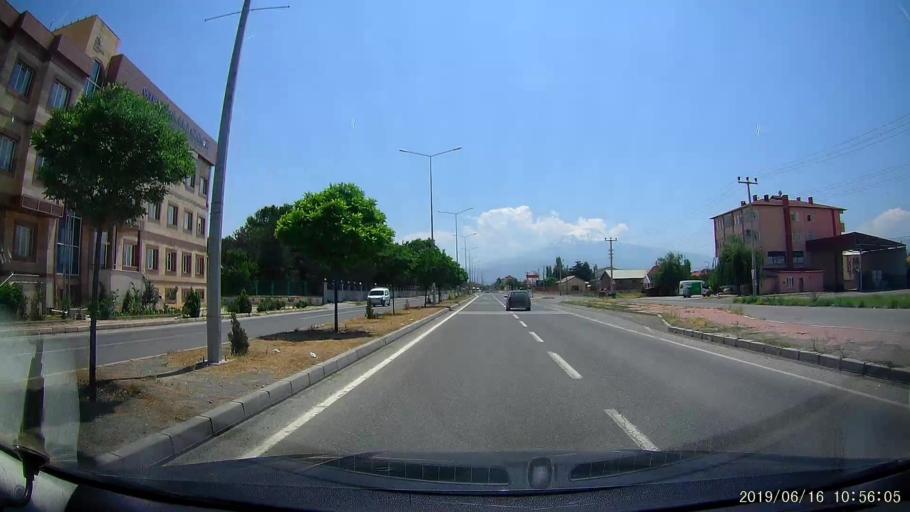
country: TR
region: Igdir
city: Igdir
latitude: 39.9325
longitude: 44.0176
